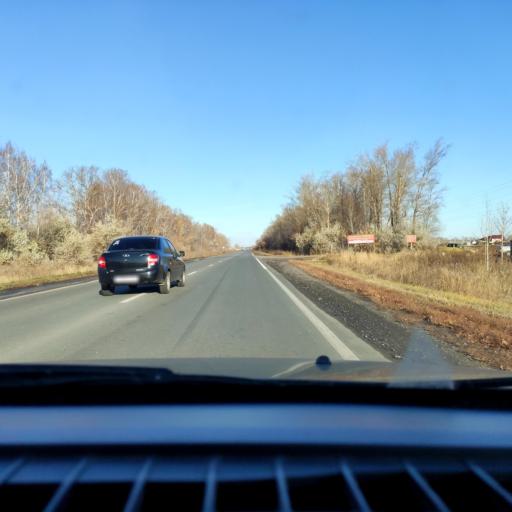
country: RU
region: Samara
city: Tol'yatti
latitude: 53.6240
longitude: 49.3074
